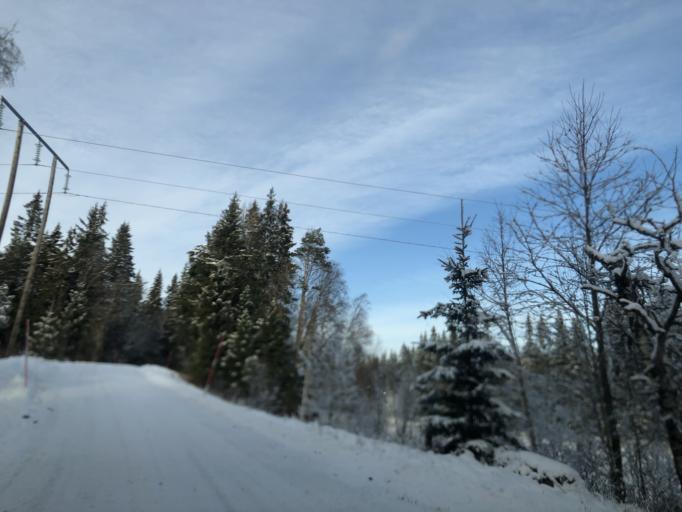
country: SE
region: Vaestra Goetaland
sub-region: Ulricehamns Kommun
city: Ulricehamn
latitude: 57.7738
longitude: 13.5235
